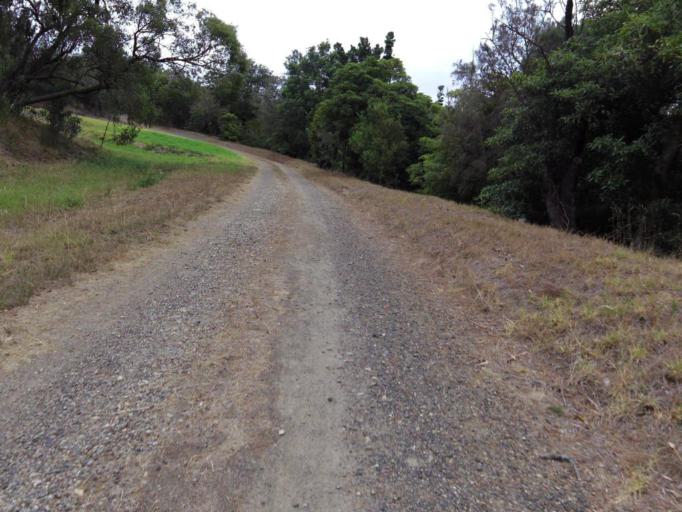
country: AU
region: Victoria
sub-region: Frankston
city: Frankston South
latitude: -38.1743
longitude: 145.1312
